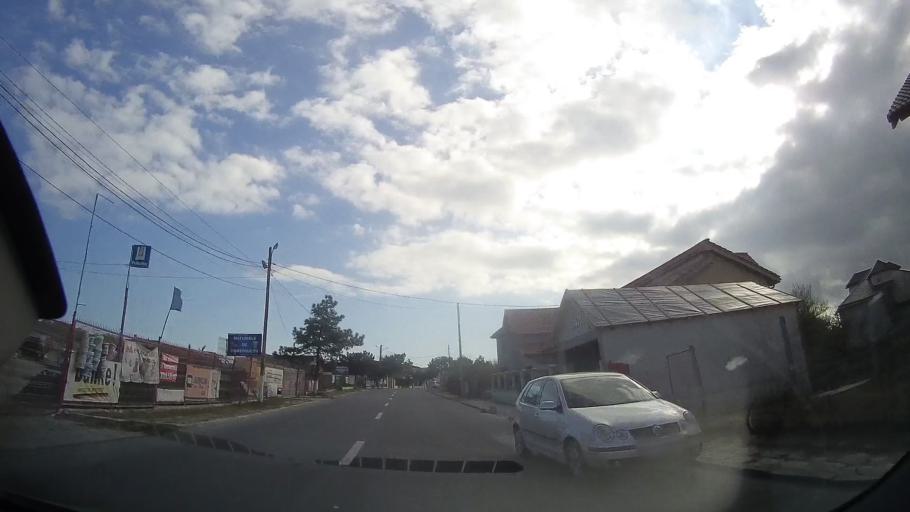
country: RO
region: Constanta
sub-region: Oras Techirghiol
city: Techirghiol
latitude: 44.0624
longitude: 28.5979
